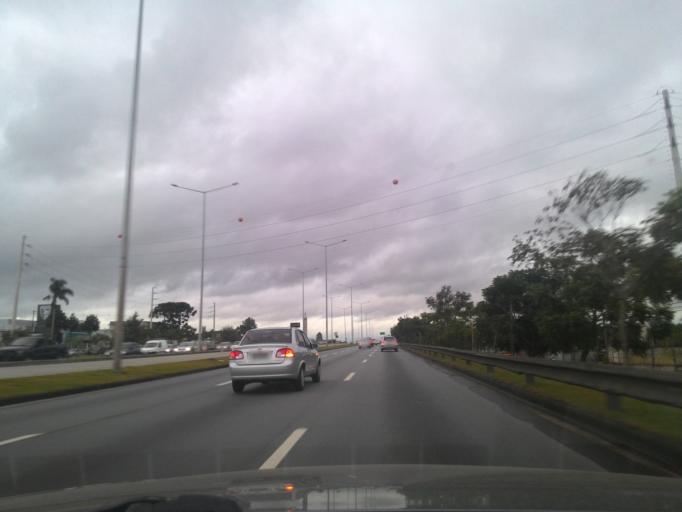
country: BR
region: Parana
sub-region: Curitiba
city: Curitiba
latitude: -25.4909
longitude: -49.2713
